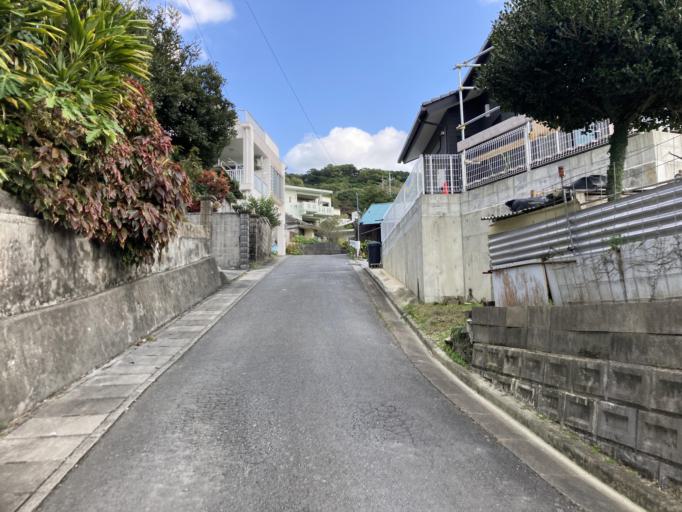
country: JP
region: Okinawa
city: Tomigusuku
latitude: 26.1867
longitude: 127.7564
